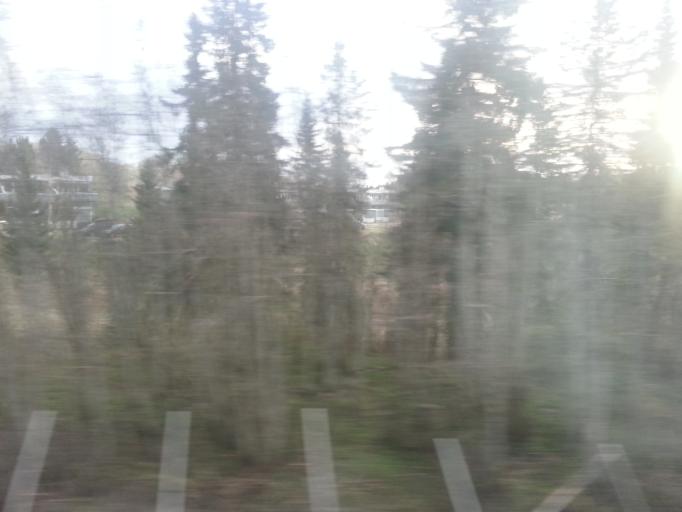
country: NO
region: Sor-Trondelag
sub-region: Trondheim
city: Trondheim
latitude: 63.3739
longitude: 10.3591
